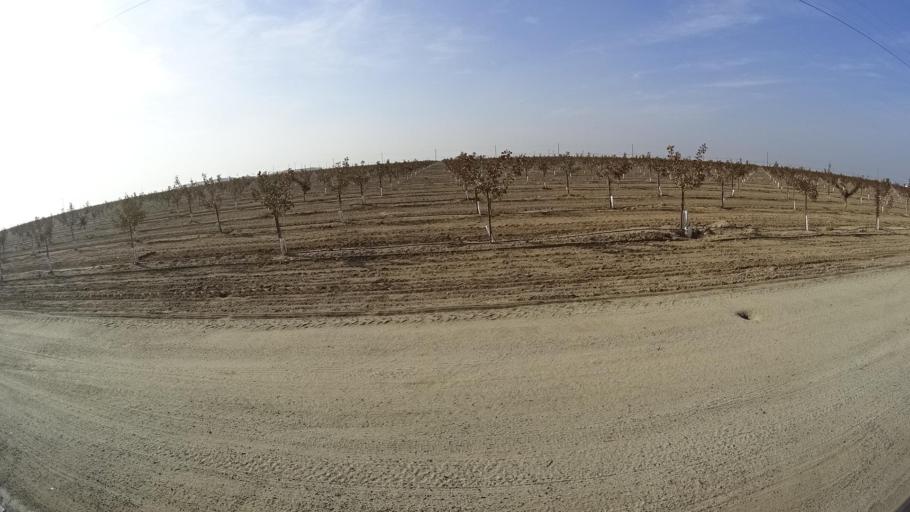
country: US
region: California
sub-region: Tulare County
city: Richgrove
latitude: 35.7788
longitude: -119.1163
